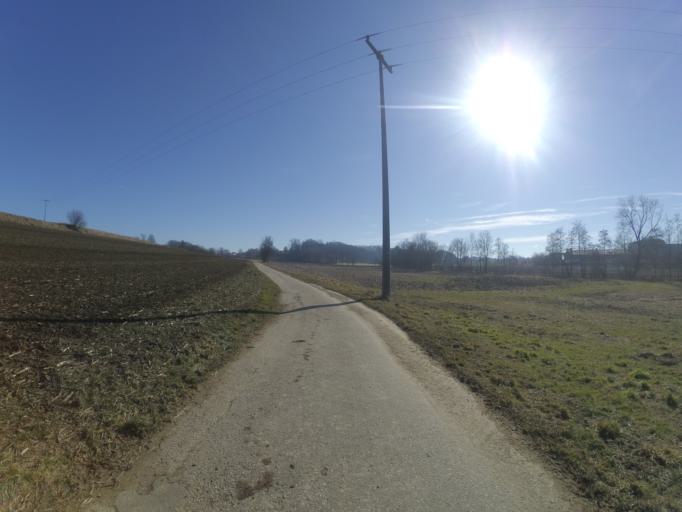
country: DE
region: Baden-Wuerttemberg
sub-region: Tuebingen Region
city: Huttisheim
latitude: 48.2931
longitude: 9.9326
